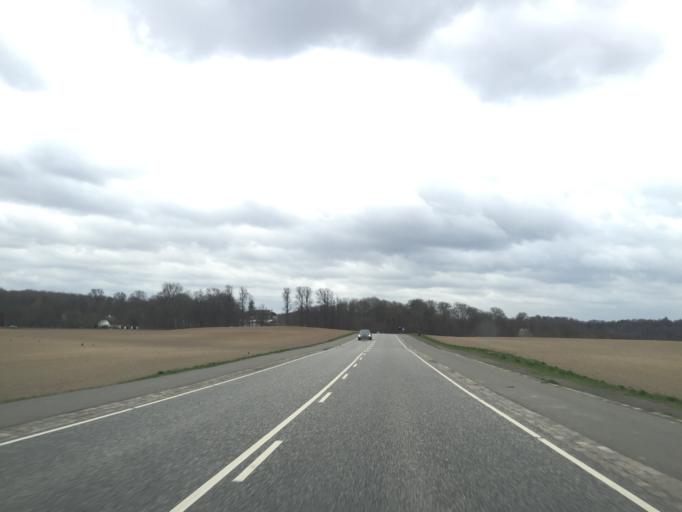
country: DK
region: Capital Region
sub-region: Rudersdal Kommune
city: Holte
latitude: 55.7875
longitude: 12.4526
